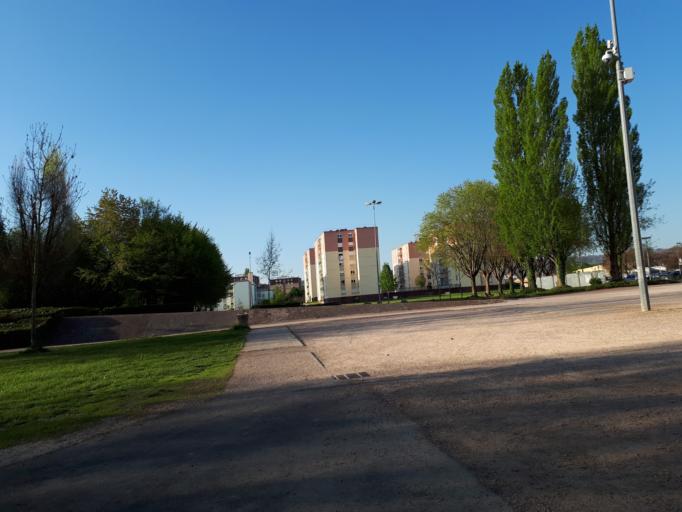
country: FR
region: Rhone-Alpes
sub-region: Departement de l'Isere
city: Bourgoin-Jallieu
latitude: 45.6100
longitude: 5.2675
